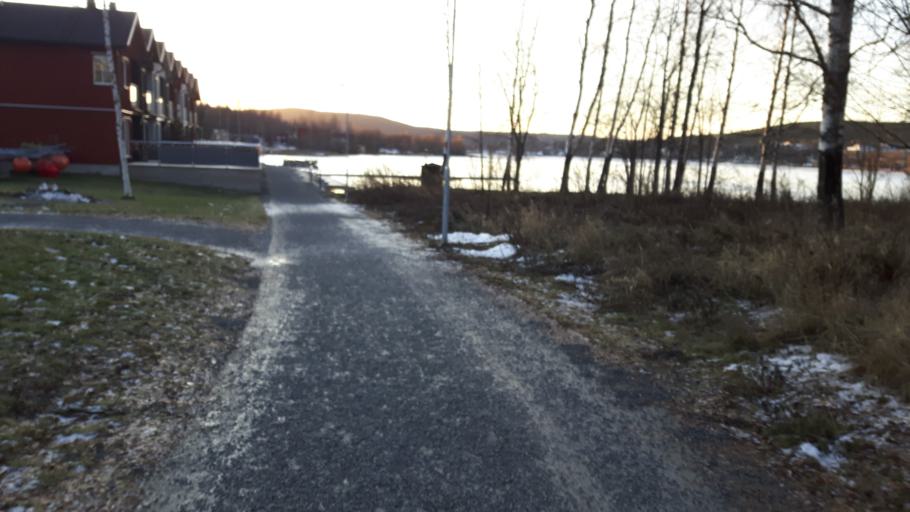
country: SE
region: Vaesternorrland
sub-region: Haernoesands Kommun
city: Haernoesand
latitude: 62.6247
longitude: 17.9485
